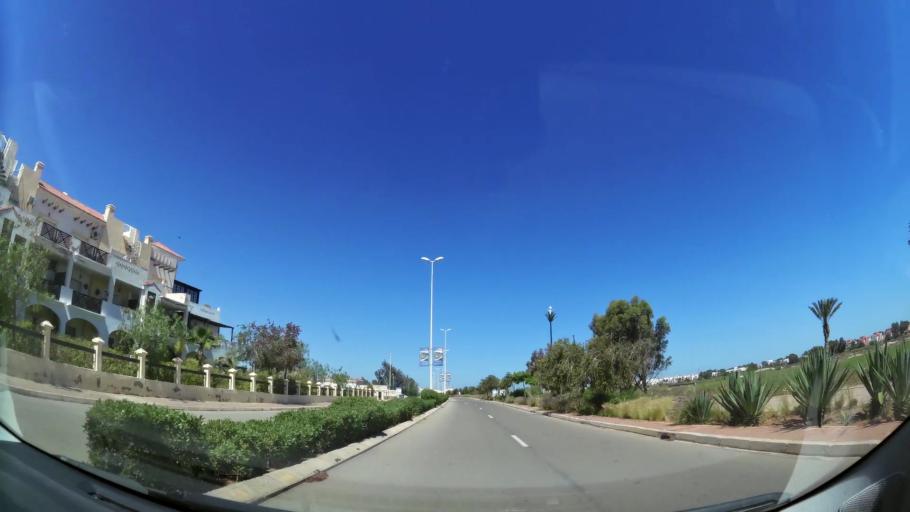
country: MA
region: Oriental
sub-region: Berkane-Taourirt
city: Madagh
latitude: 35.1025
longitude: -2.3045
